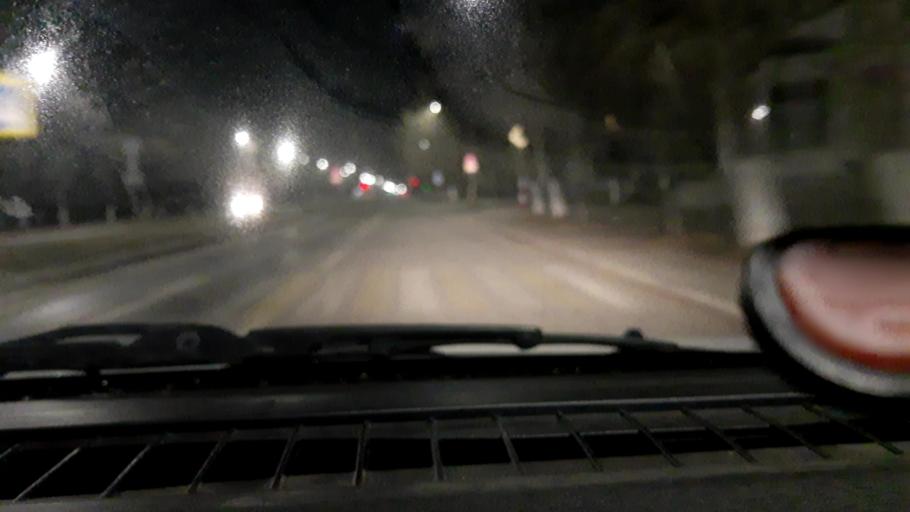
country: RU
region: Nizjnij Novgorod
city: Dzerzhinsk
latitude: 56.2386
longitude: 43.4557
